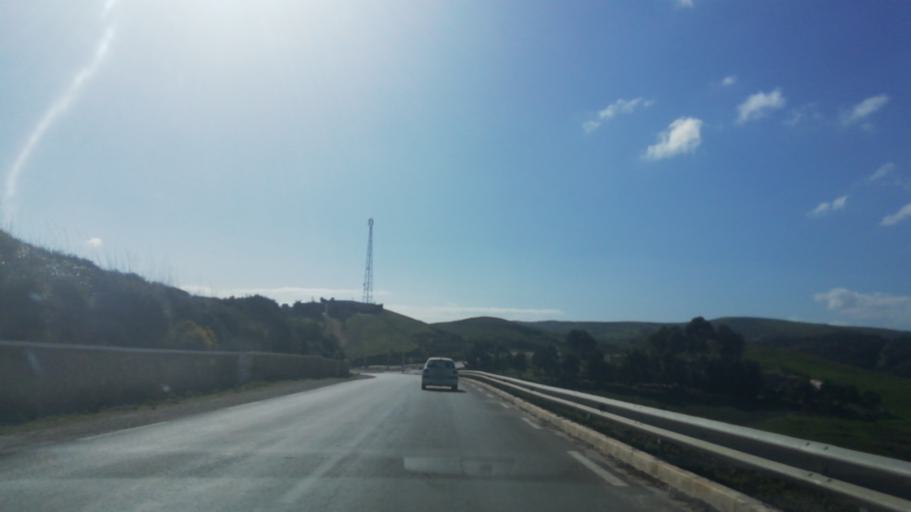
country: DZ
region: Relizane
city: Relizane
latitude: 36.0828
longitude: 0.4987
